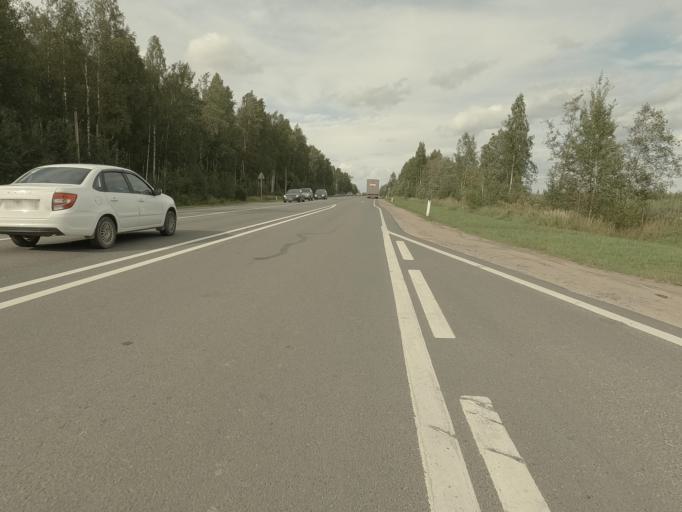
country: RU
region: Leningrad
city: Mga
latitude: 59.7856
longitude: 31.1060
